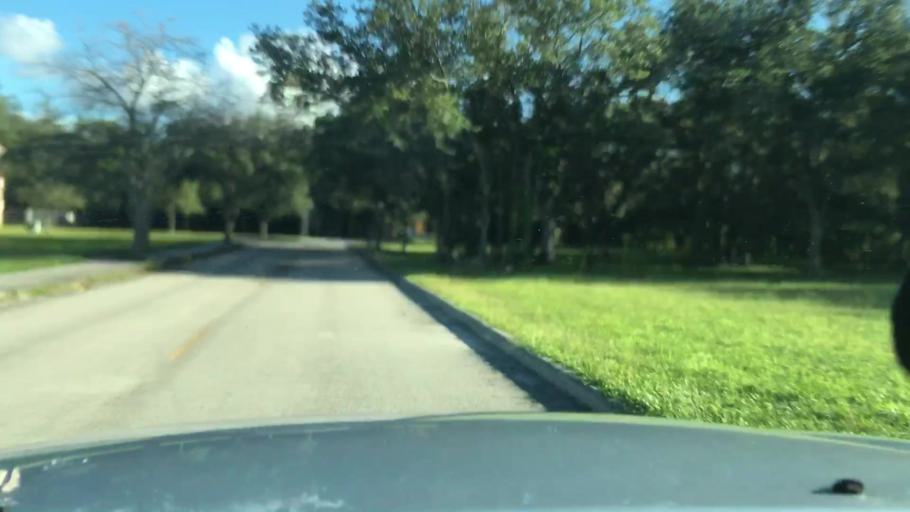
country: US
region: Florida
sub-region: Miami-Dade County
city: Sunset
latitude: 25.6919
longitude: -80.3684
